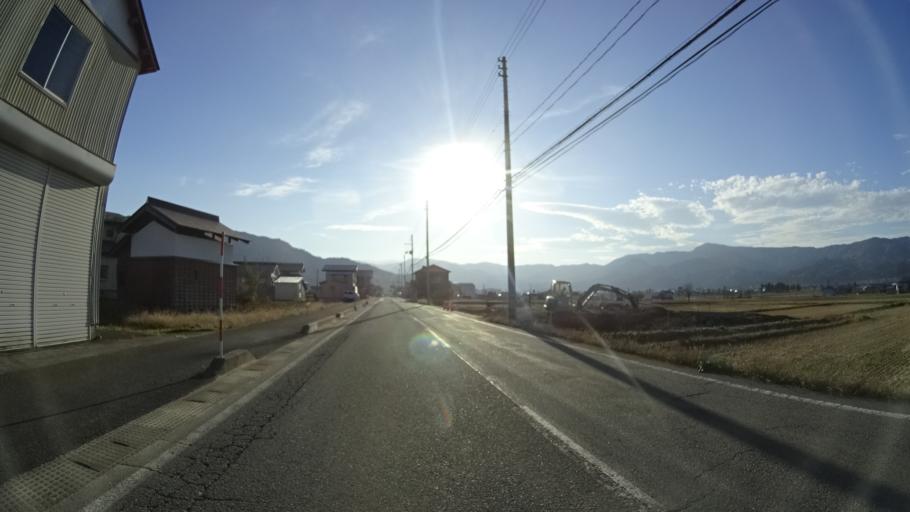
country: JP
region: Niigata
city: Shiozawa
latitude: 37.0189
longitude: 138.8606
